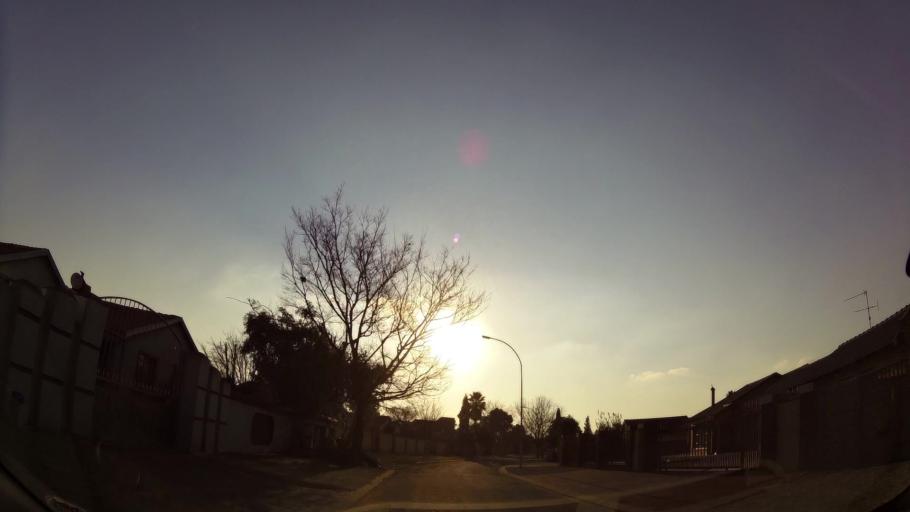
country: ZA
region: Gauteng
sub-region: Ekurhuleni Metropolitan Municipality
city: Benoni
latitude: -26.1228
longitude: 28.3782
